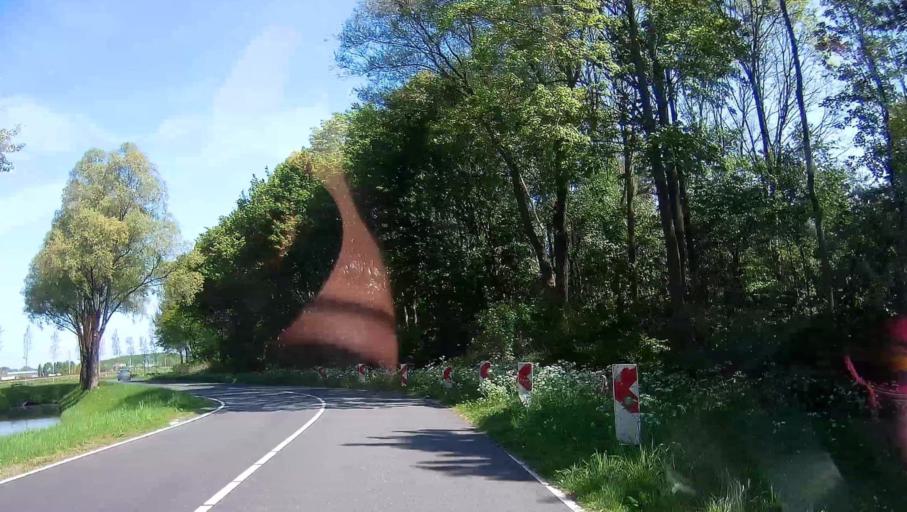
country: NL
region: South Holland
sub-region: Gemeente Pijnacker-Nootdorp
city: Pijnacker
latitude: 52.0596
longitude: 4.4453
